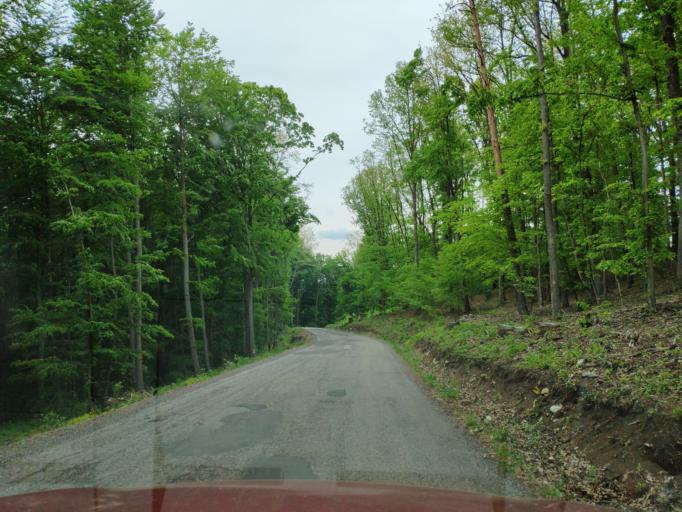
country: SK
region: Banskobystricky
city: Revuca
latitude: 48.5264
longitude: 20.1115
